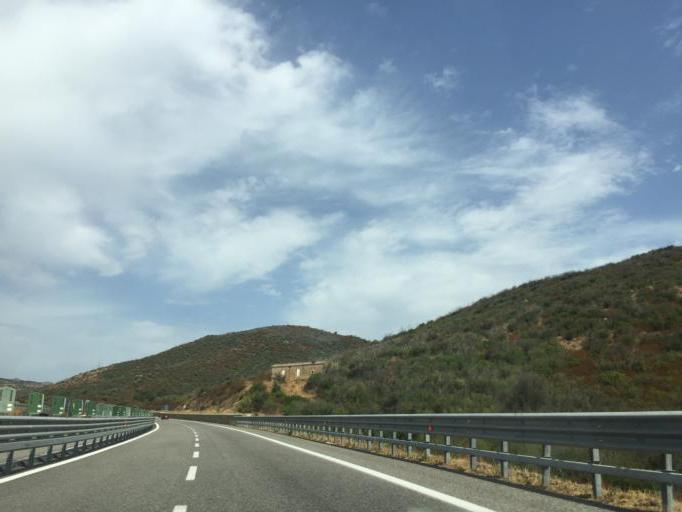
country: IT
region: Sardinia
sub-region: Provincia di Olbia-Tempio
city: San Teodoro
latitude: 40.7696
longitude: 9.6378
